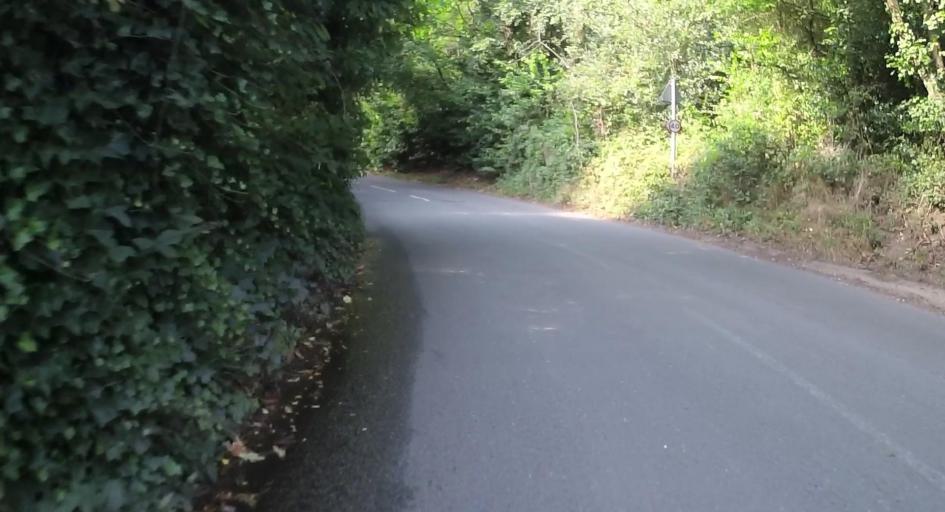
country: GB
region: England
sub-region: Surrey
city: Farnham
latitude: 51.1786
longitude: -0.7959
